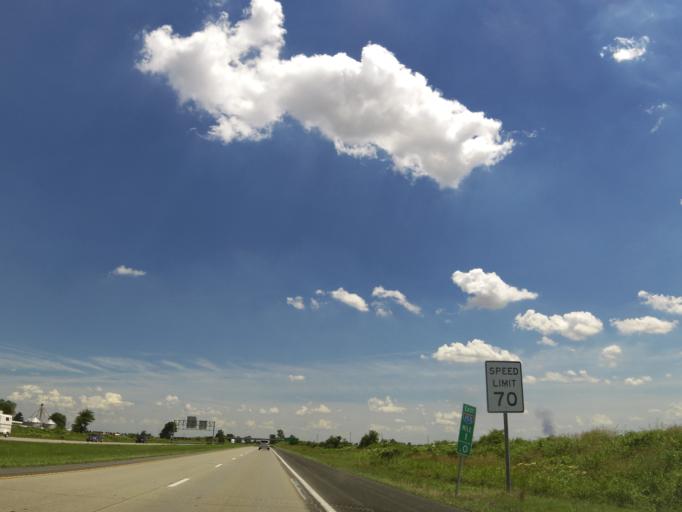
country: US
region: Missouri
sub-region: Pemiscot County
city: Hayti
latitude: 36.2061
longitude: -89.7370
